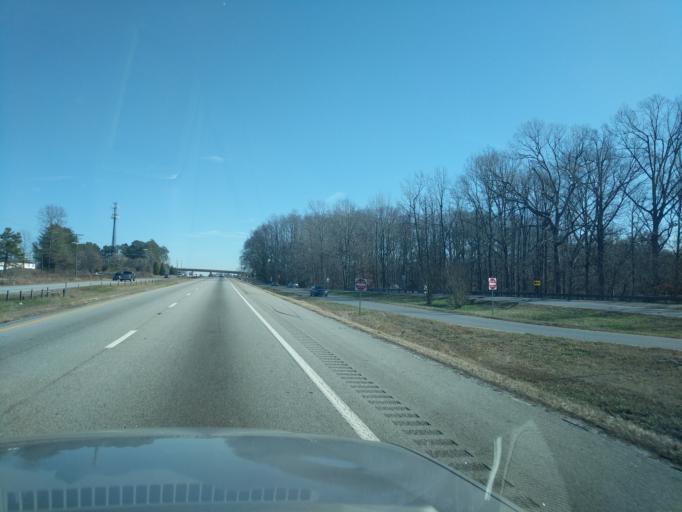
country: US
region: South Carolina
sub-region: Spartanburg County
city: Fairforest
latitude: 34.9642
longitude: -82.0269
